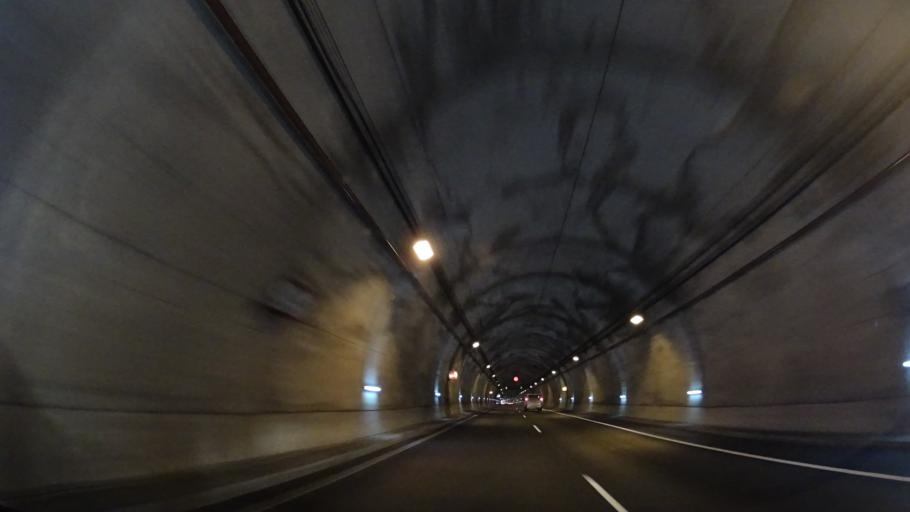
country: ES
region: Asturias
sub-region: Province of Asturias
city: Ribadesella
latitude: 43.4664
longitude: -5.1493
